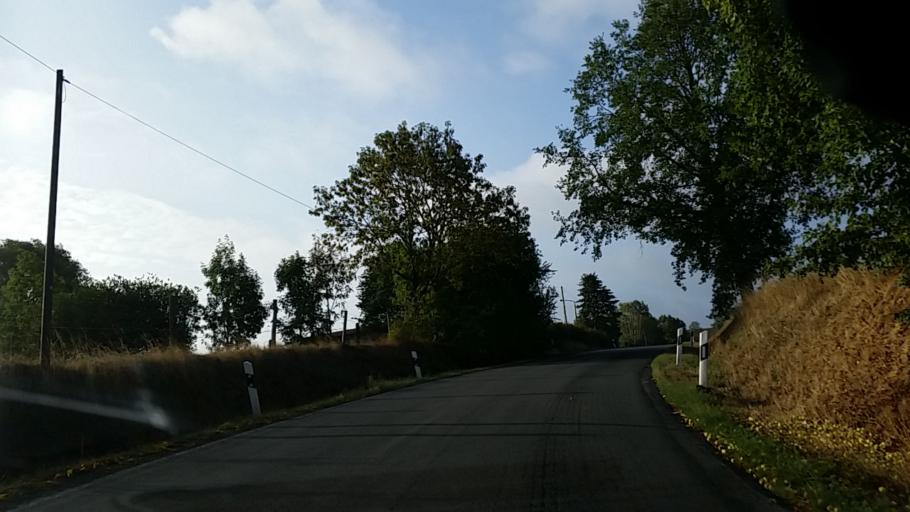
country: DE
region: Lower Saxony
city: Bad Sachsa
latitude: 51.5489
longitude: 10.5534
